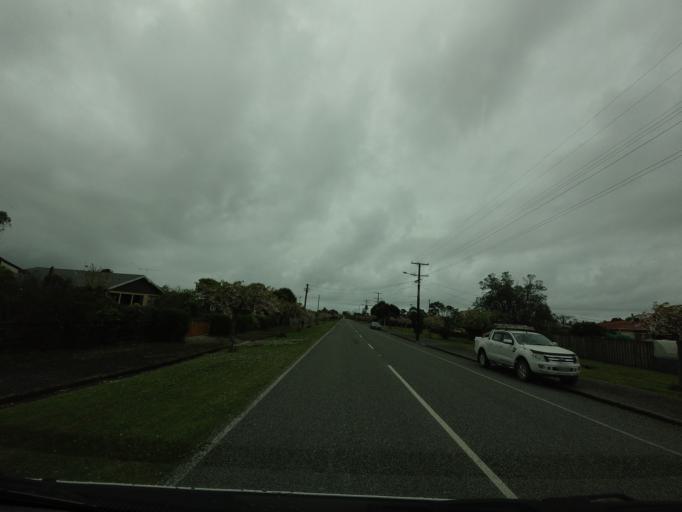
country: NZ
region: West Coast
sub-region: Westland District
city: Hokitika
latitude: -42.8956
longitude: 170.8138
